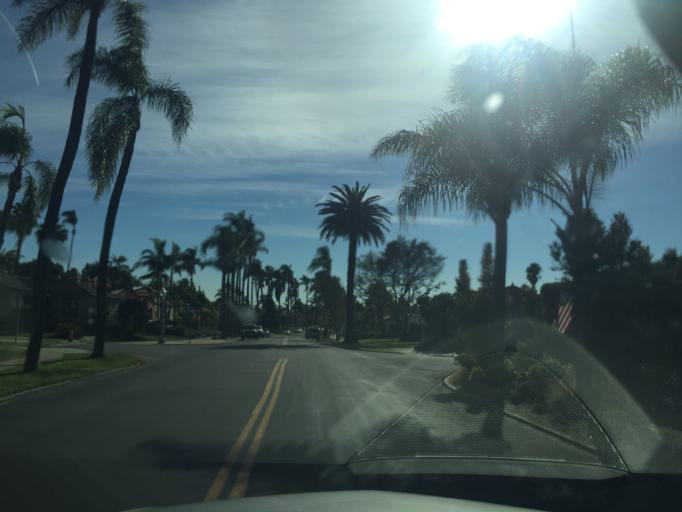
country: US
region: California
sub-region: San Diego County
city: San Diego
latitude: 32.7689
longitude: -117.1064
